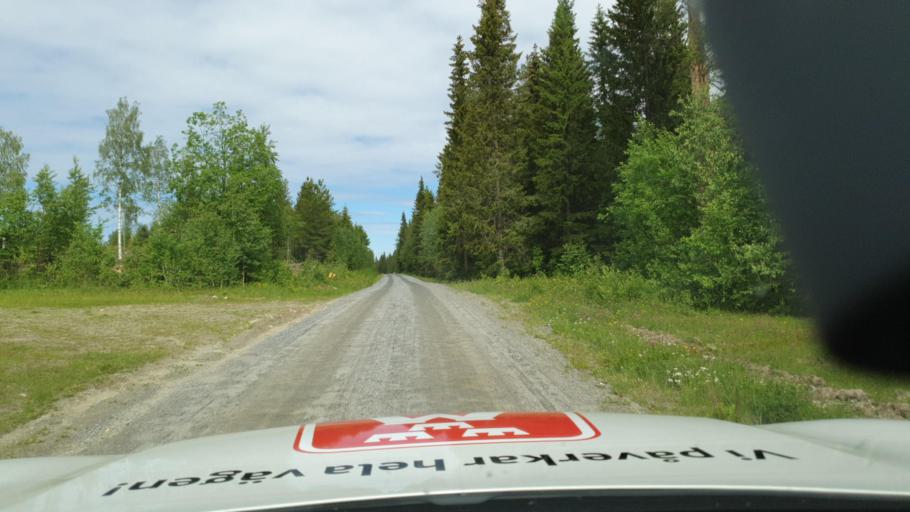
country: SE
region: Vaesterbotten
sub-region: Skelleftea Kommun
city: Langsele
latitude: 64.6207
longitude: 20.2641
